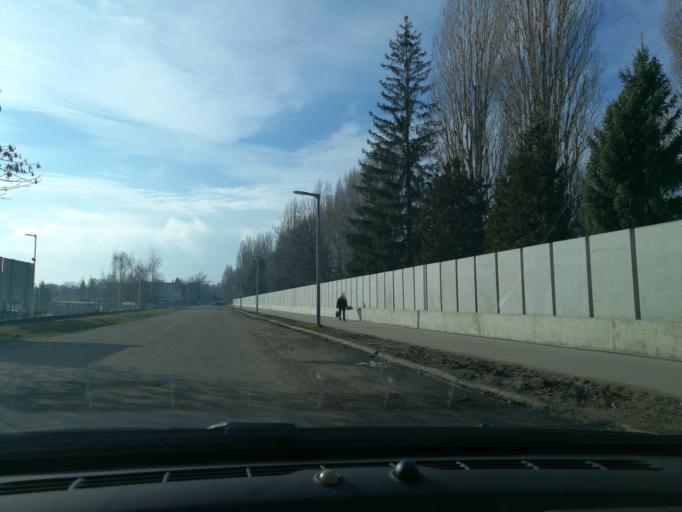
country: HU
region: Szabolcs-Szatmar-Bereg
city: Nyiregyhaza
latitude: 47.9655
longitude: 21.7269
